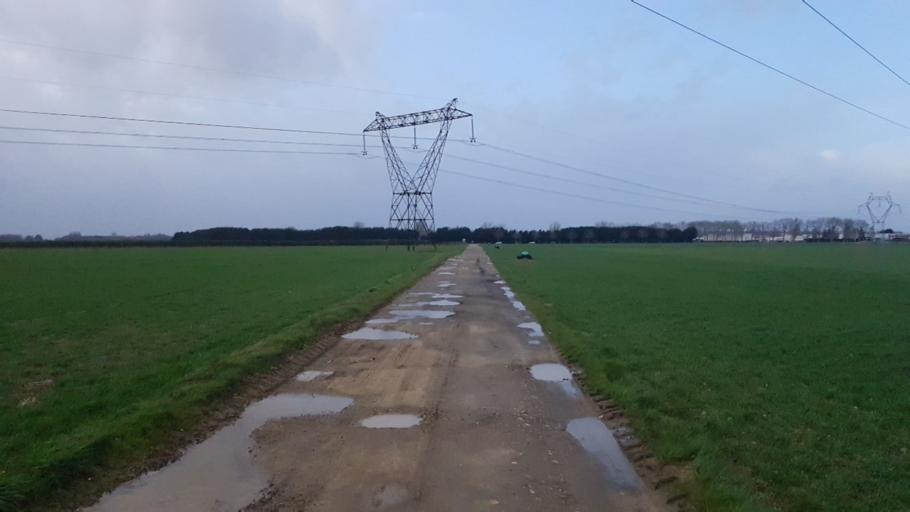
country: FR
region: Ile-de-France
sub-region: Departement de l'Essonne
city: Cheptainville
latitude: 48.5621
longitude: 2.2794
